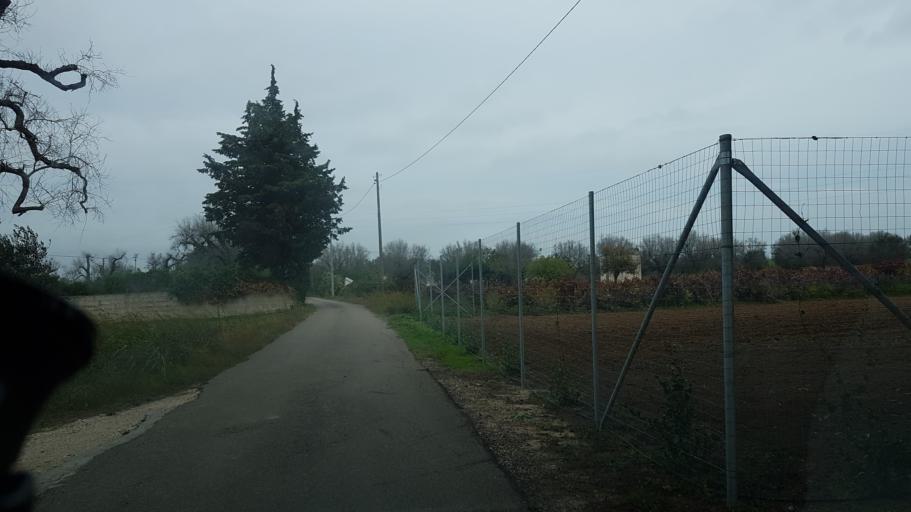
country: IT
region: Apulia
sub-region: Provincia di Brindisi
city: San Donaci
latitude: 40.4531
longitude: 17.9354
